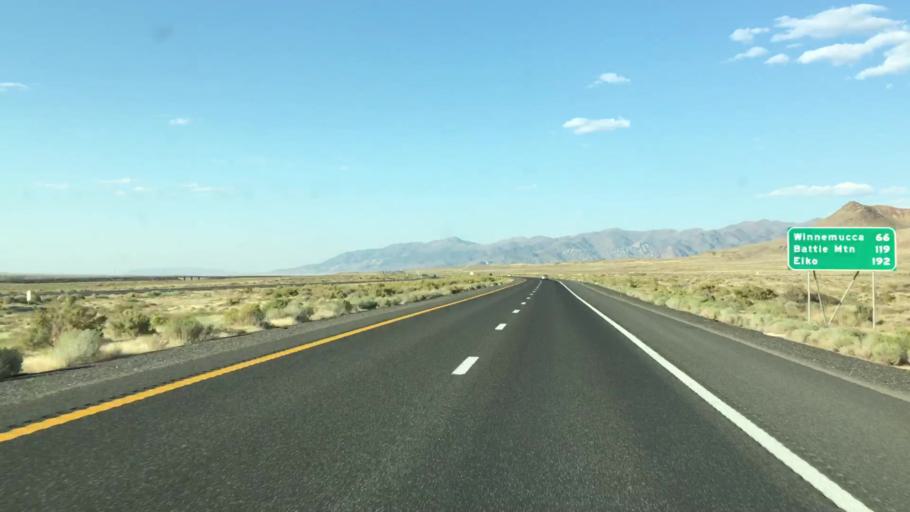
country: US
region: Nevada
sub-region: Pershing County
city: Lovelock
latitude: 40.2529
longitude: -118.3785
